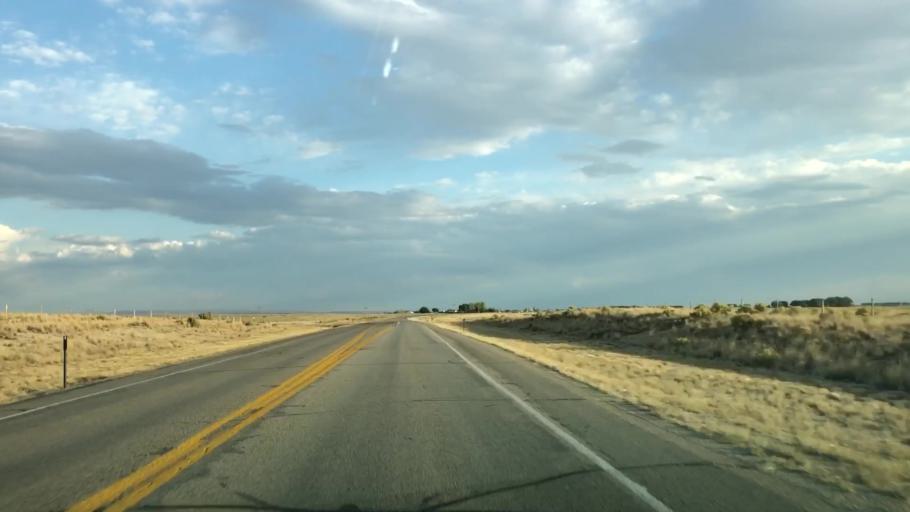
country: US
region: Wyoming
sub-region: Sweetwater County
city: North Rock Springs
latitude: 42.0912
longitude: -109.4414
